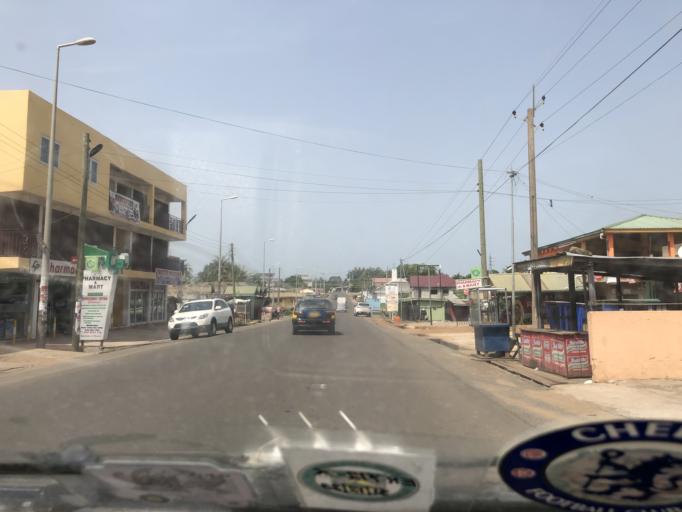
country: GH
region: Eastern
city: Koforidua
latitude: 6.0967
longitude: -0.2664
